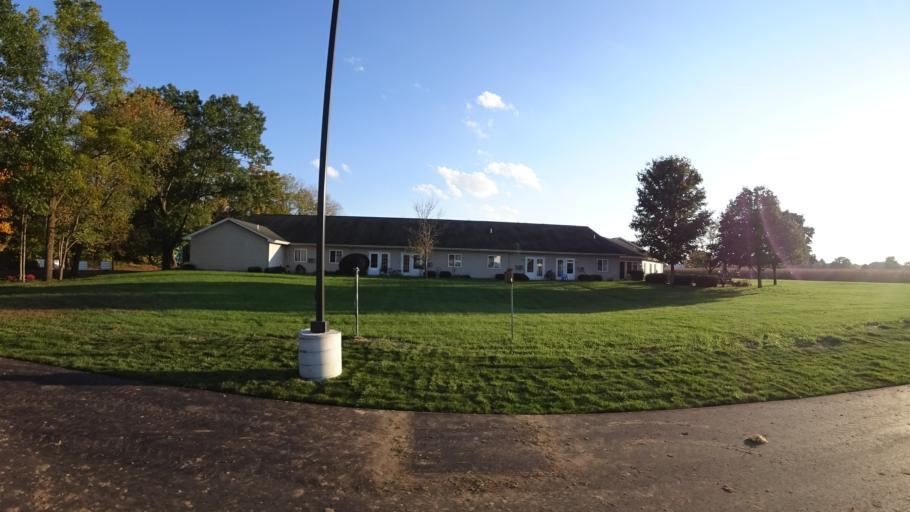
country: US
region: Michigan
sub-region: Saint Joseph County
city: Three Rivers
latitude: 41.9510
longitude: -85.6437
